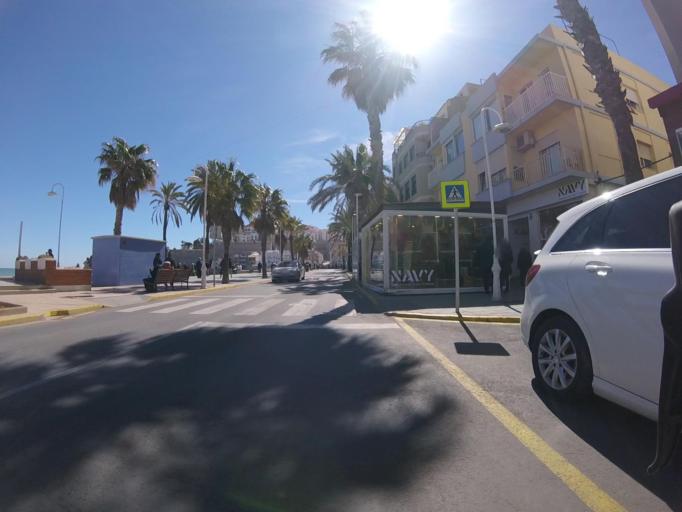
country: ES
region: Valencia
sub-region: Provincia de Castello
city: Peniscola
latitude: 40.3599
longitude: 0.4037
